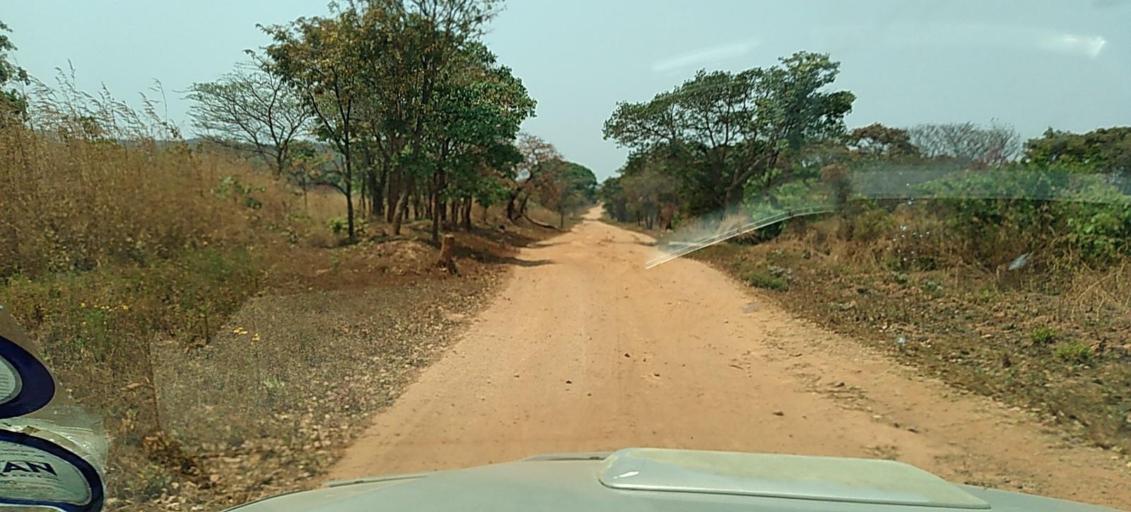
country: ZM
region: North-Western
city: Kasempa
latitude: -13.5507
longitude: 26.0188
